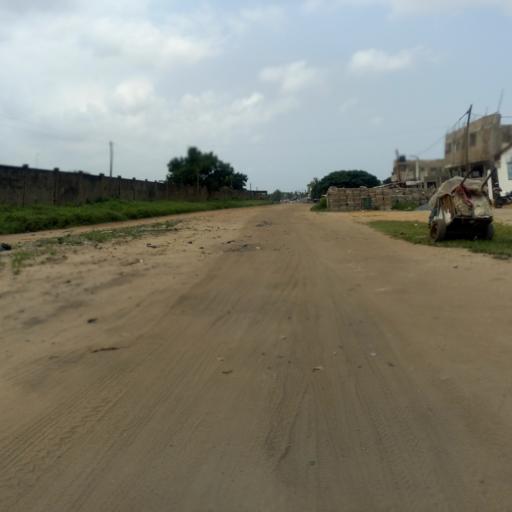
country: TG
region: Maritime
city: Lome
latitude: 6.1856
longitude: 1.1680
